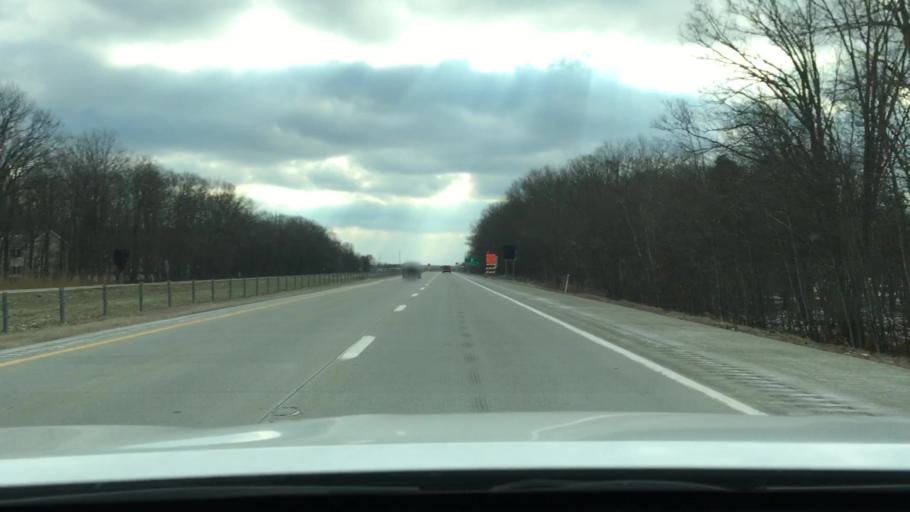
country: US
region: Pennsylvania
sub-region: Monroe County
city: Emerald Lakes
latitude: 41.1138
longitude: -75.3989
